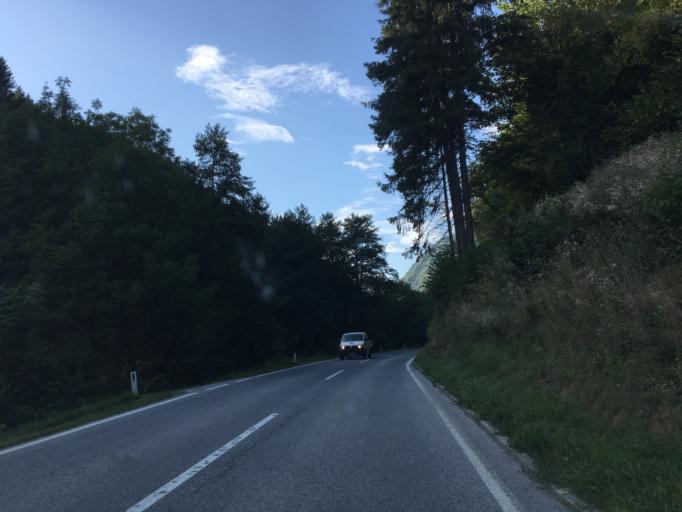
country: AT
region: Carinthia
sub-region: Politischer Bezirk Sankt Veit an der Glan
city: Bruckl
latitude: 46.7081
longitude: 14.5662
